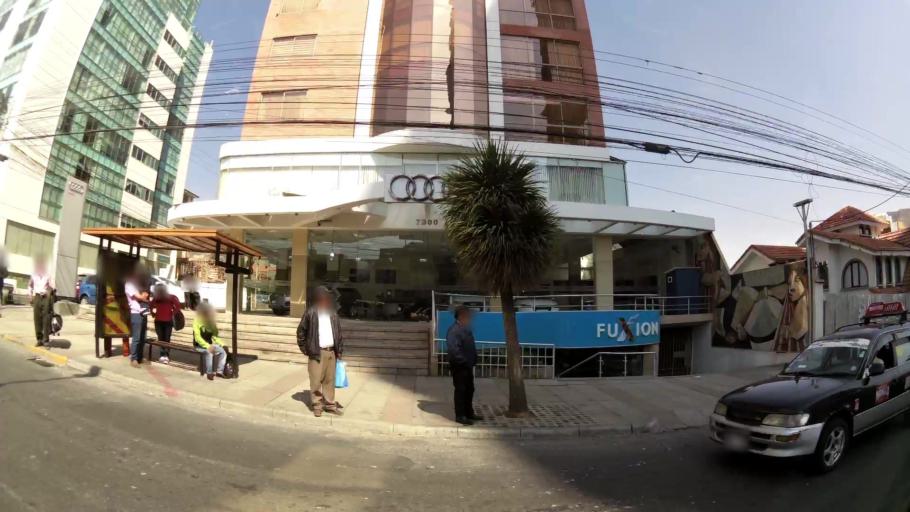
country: BO
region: La Paz
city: La Paz
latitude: -16.5402
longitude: -68.0875
